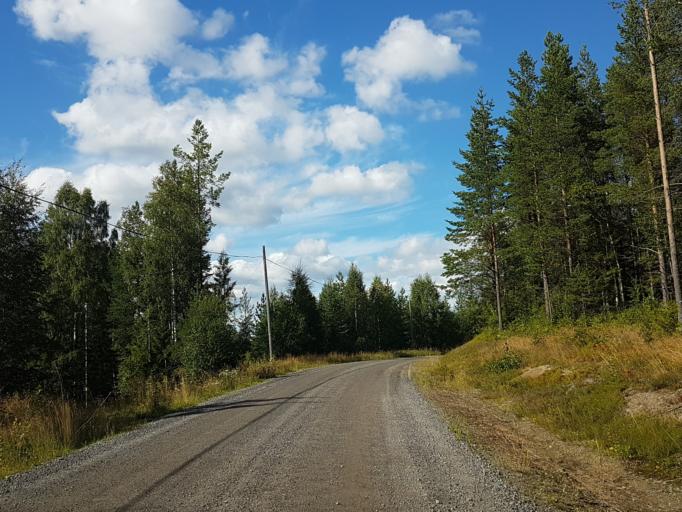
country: SE
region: Vaesterbotten
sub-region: Skelleftea Kommun
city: Burtraesk
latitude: 64.2755
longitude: 20.4799
